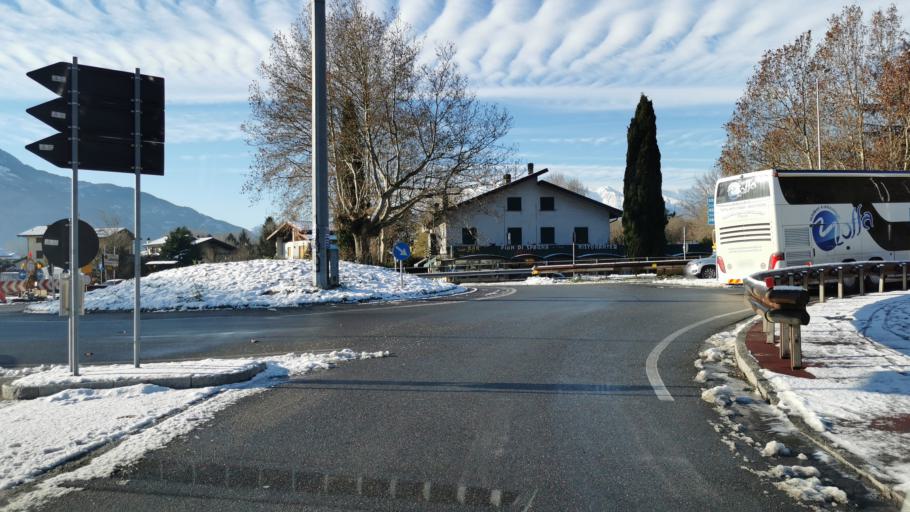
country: IT
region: Lombardy
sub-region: Provincia di Como
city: Sorico
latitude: 46.1719
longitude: 9.4050
